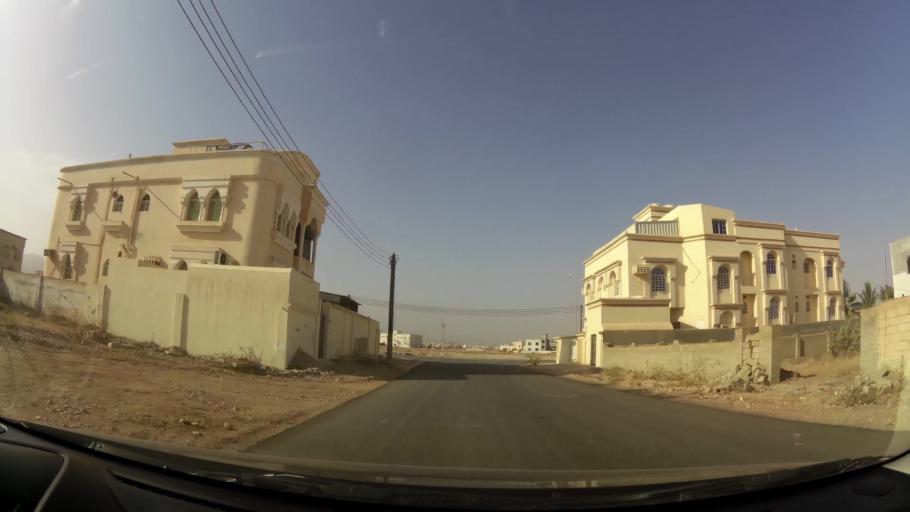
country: OM
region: Zufar
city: Salalah
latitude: 17.0171
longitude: 54.0130
